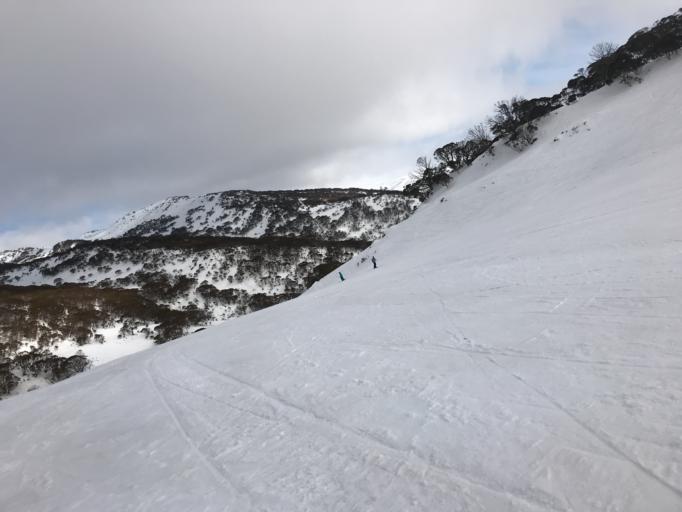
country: AU
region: New South Wales
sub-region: Snowy River
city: Jindabyne
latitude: -36.3832
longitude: 148.3795
